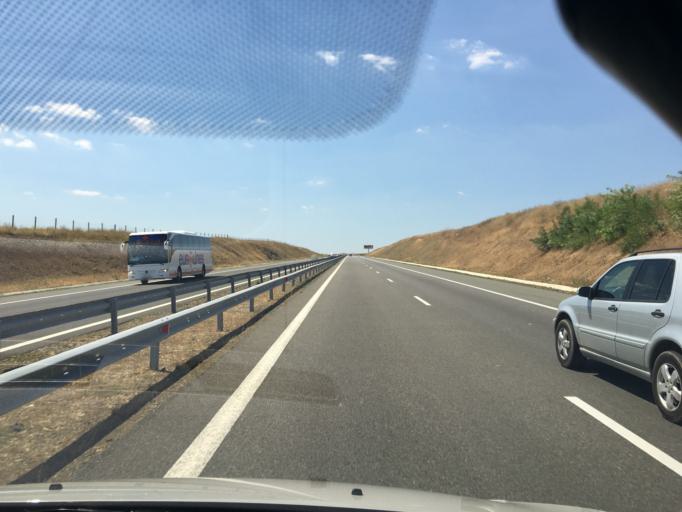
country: BG
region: Burgas
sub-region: Obshtina Karnobat
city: Karnobat
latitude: 42.5887
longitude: 26.9608
